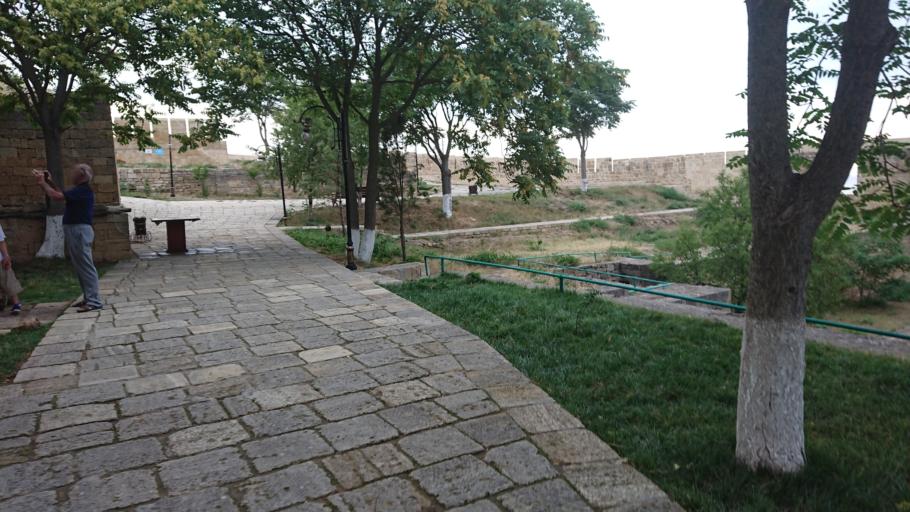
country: RU
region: Dagestan
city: Derbent
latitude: 42.0534
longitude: 48.2746
